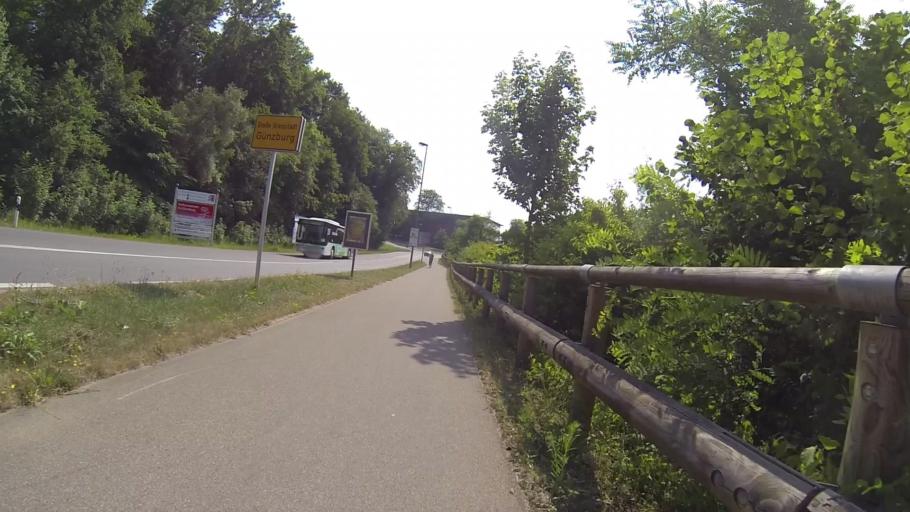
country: DE
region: Bavaria
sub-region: Swabia
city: Guenzburg
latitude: 48.4613
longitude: 10.2843
